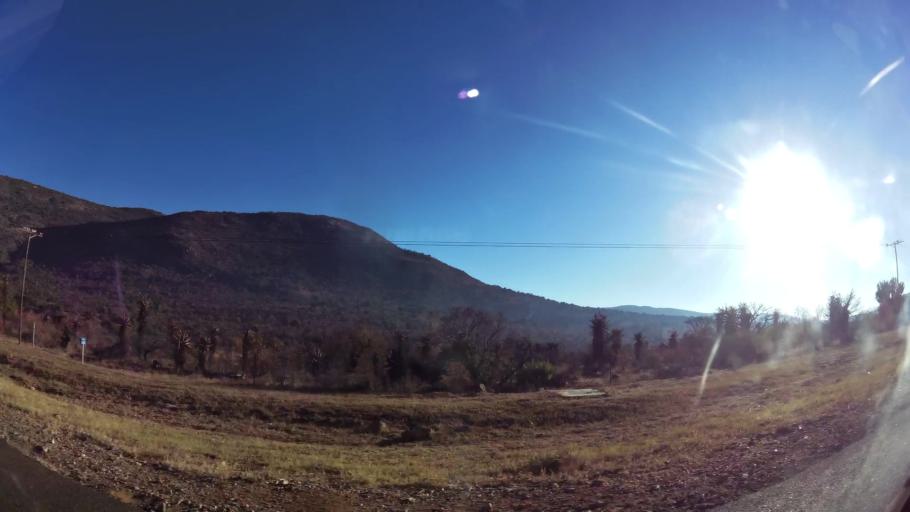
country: ZA
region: Limpopo
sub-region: Capricorn District Municipality
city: Mankoeng
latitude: -23.9434
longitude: 29.8149
